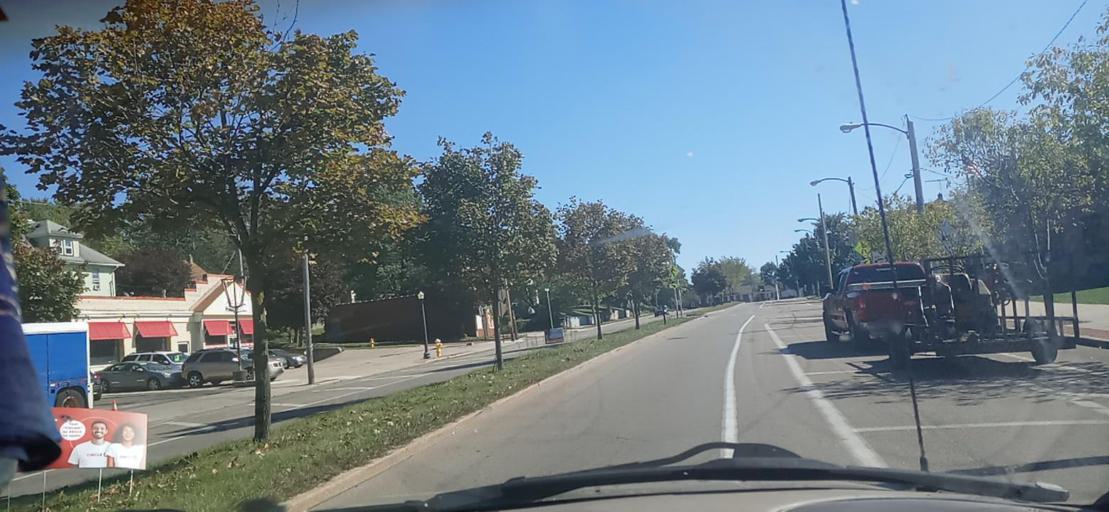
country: US
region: Ohio
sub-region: Summit County
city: Portage Lakes
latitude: 41.0437
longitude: -81.5562
